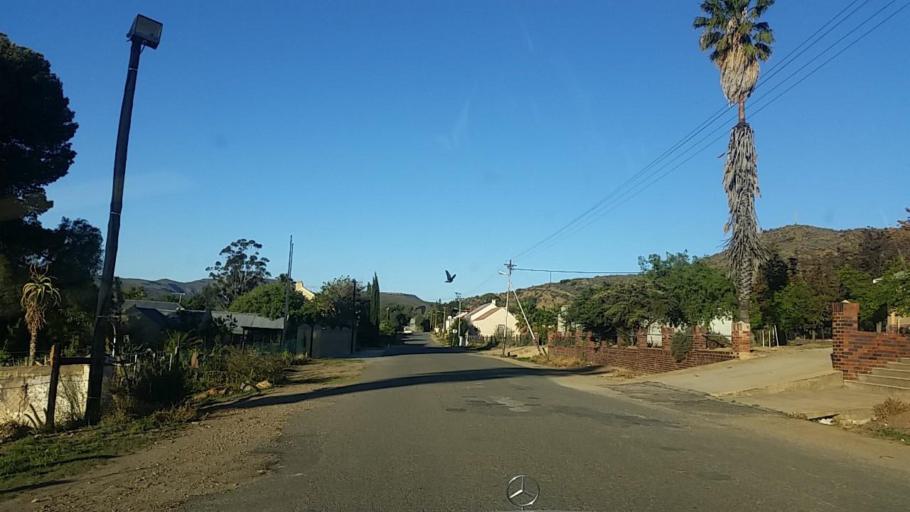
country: ZA
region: Western Cape
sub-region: Eden District Municipality
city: Knysna
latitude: -33.6578
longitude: 23.1268
